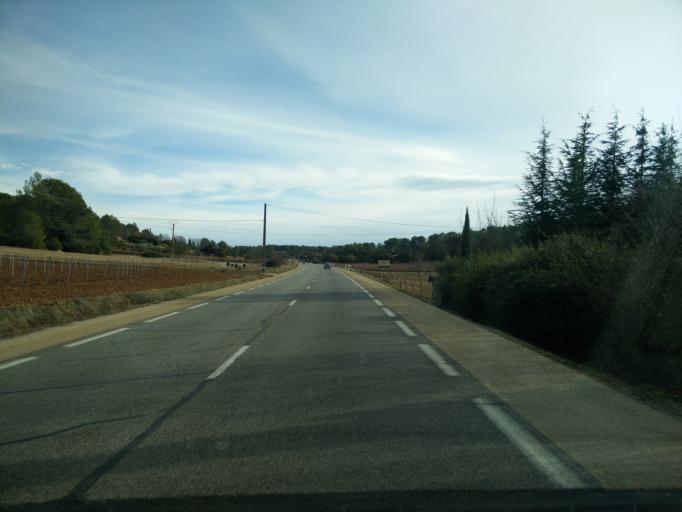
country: FR
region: Provence-Alpes-Cote d'Azur
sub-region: Departement du Var
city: Lorgues
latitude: 43.4707
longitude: 6.3815
